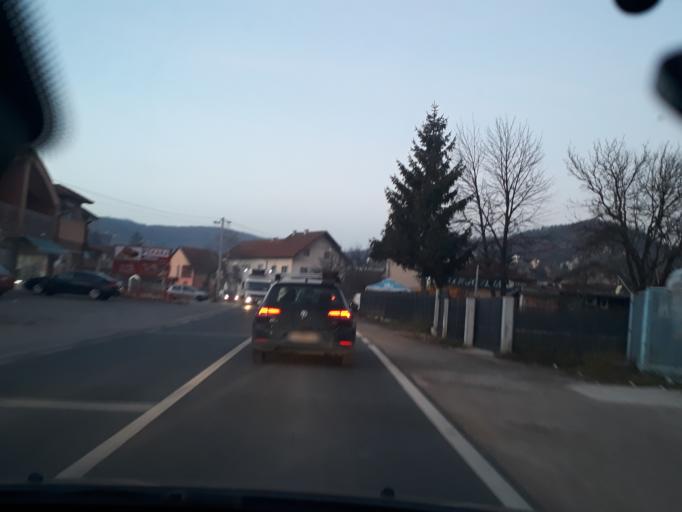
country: BA
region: Federation of Bosnia and Herzegovina
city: Hadzici
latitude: 43.8767
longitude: 18.2062
